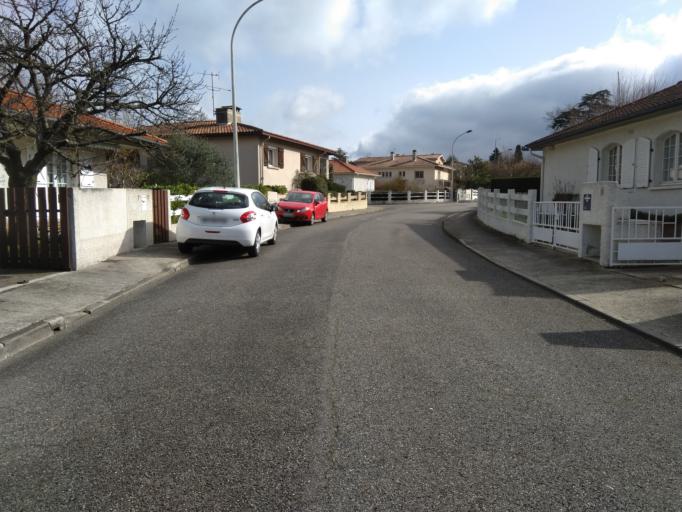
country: FR
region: Midi-Pyrenees
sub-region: Departement de la Haute-Garonne
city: Ramonville-Saint-Agne
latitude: 43.5475
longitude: 1.4647
